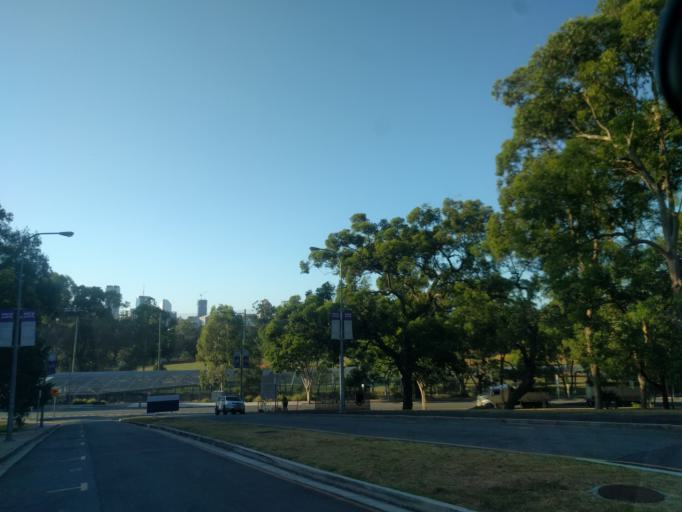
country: AU
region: Queensland
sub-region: Brisbane
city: Fortitude Valley
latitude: -27.4487
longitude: 153.0241
